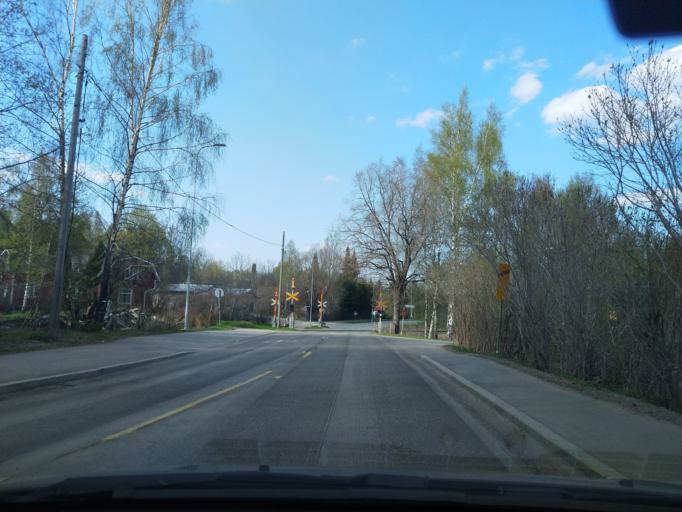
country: FI
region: Uusimaa
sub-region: Helsinki
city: Lohja
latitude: 60.1945
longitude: 24.0021
